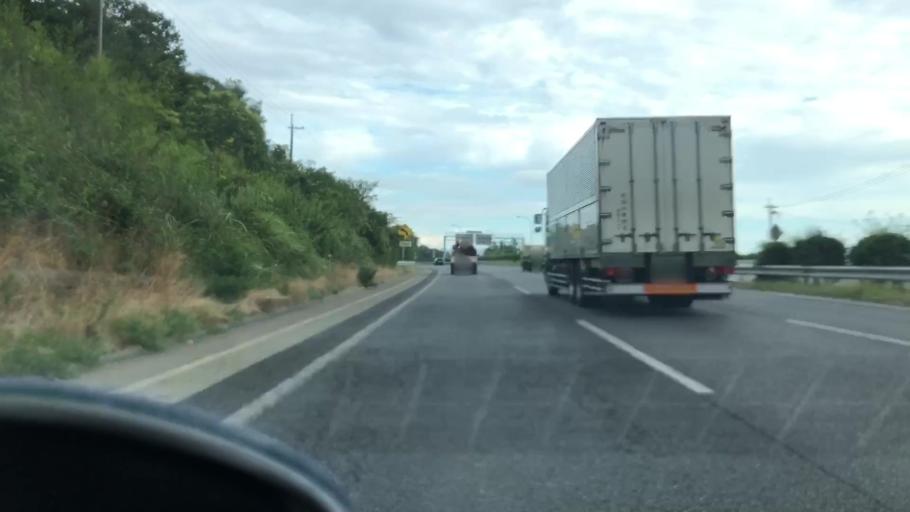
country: JP
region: Hyogo
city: Sandacho
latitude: 34.8884
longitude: 135.1612
